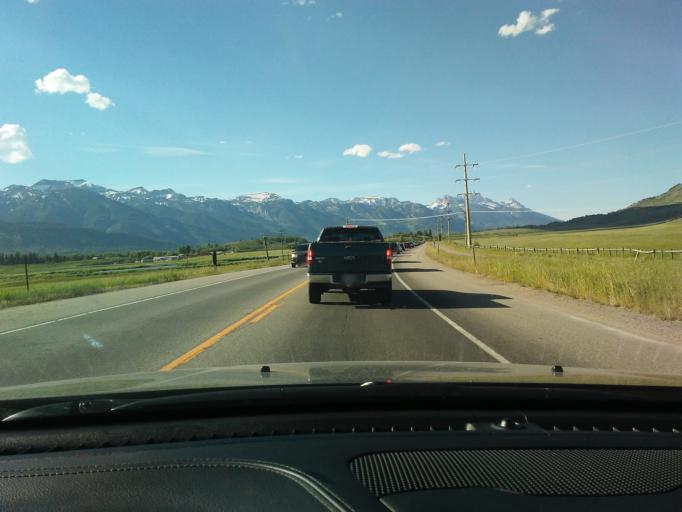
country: US
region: Wyoming
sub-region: Teton County
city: Moose Wilson Road
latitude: 43.4858
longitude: -110.8272
